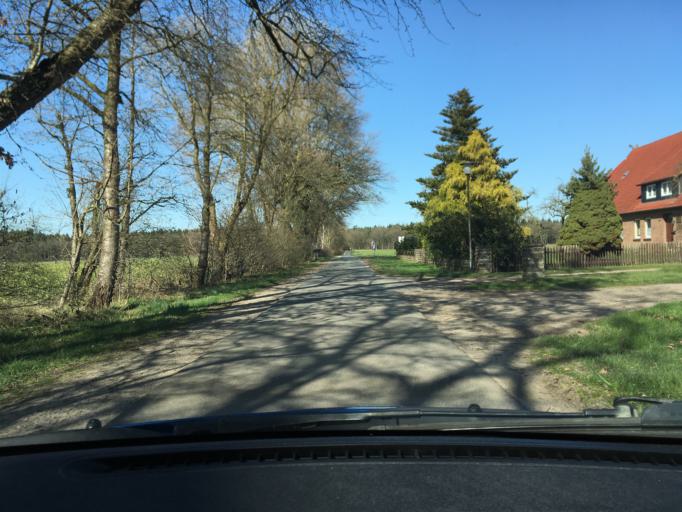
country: DE
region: Lower Saxony
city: Schwienau
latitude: 53.0255
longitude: 10.4448
